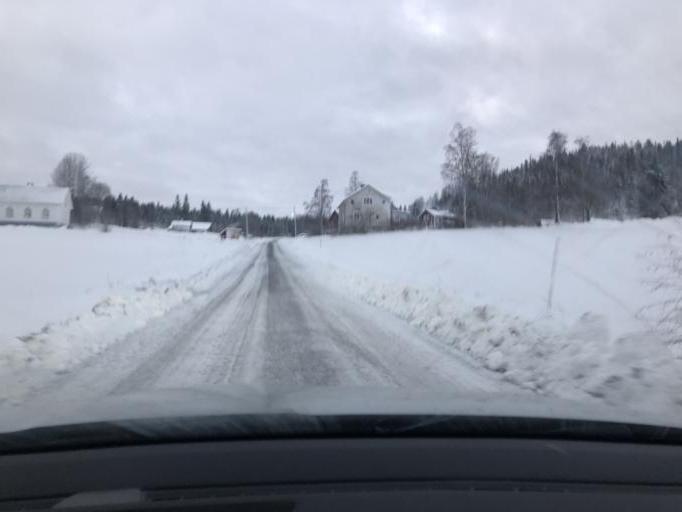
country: SE
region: Vaesternorrland
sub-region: Kramfors Kommun
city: Nordingra
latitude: 62.9132
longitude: 18.2341
